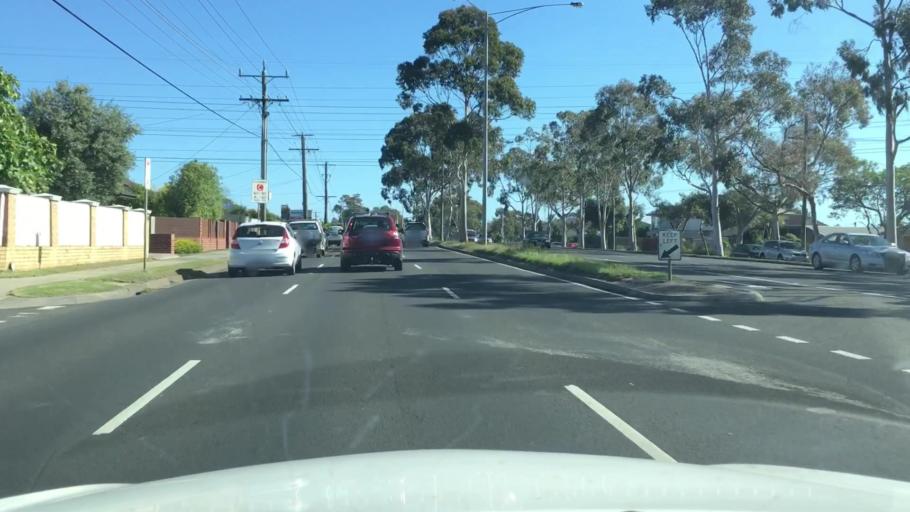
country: AU
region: Victoria
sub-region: Monash
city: Notting Hill
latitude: -37.8941
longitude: 145.1634
